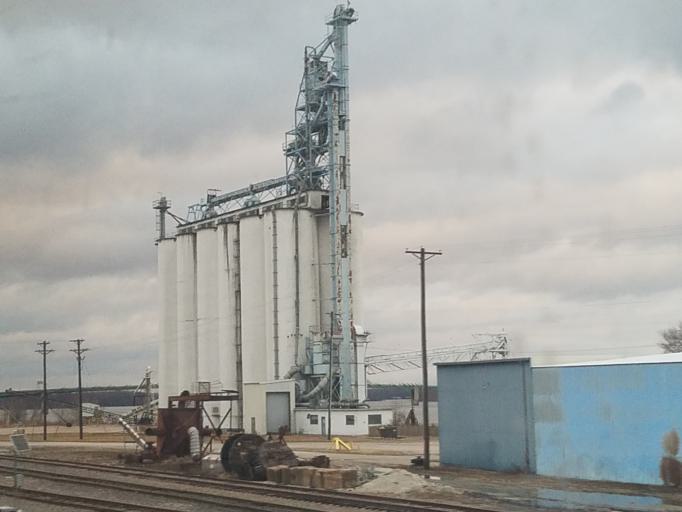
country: US
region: Iowa
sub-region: Des Moines County
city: Burlington
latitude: 40.8010
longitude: -91.0999
